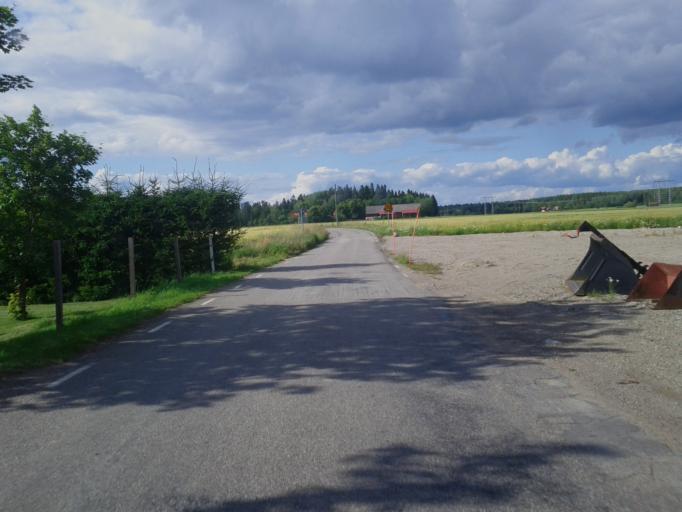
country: SE
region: Vaestmanland
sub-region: Sala Kommun
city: Sala
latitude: 59.9185
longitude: 16.5045
